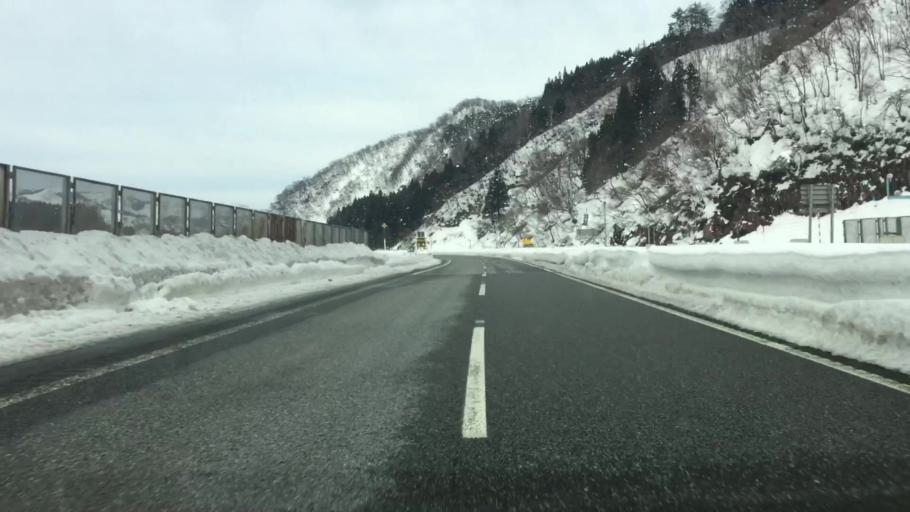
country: JP
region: Niigata
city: Shiozawa
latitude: 36.9548
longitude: 138.8028
